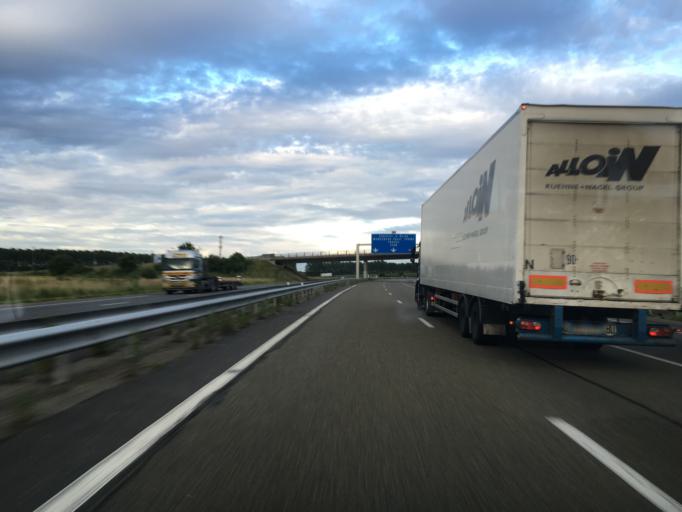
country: FR
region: Ile-de-France
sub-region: Departement de Seine-et-Marne
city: Moisenay
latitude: 48.5874
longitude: 2.7177
